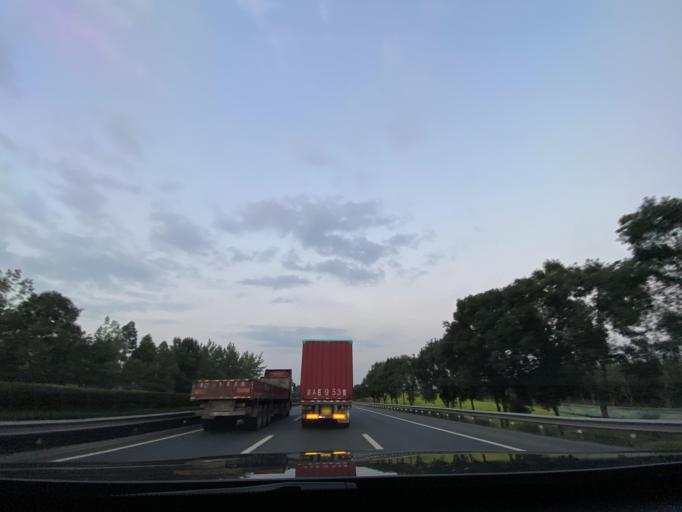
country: CN
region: Sichuan
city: Chengdu
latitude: 30.5710
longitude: 104.1238
